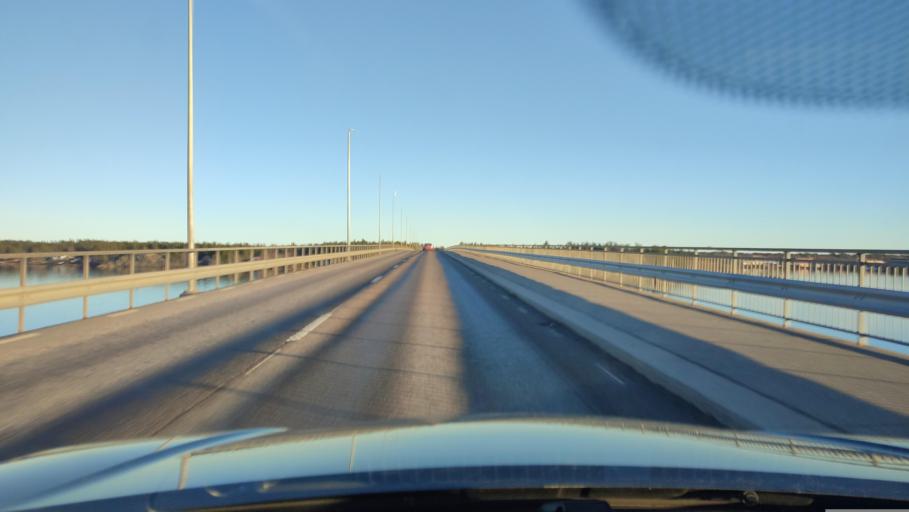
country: SE
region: Vaesterbotten
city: Obbola
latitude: 63.7093
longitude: 20.3313
